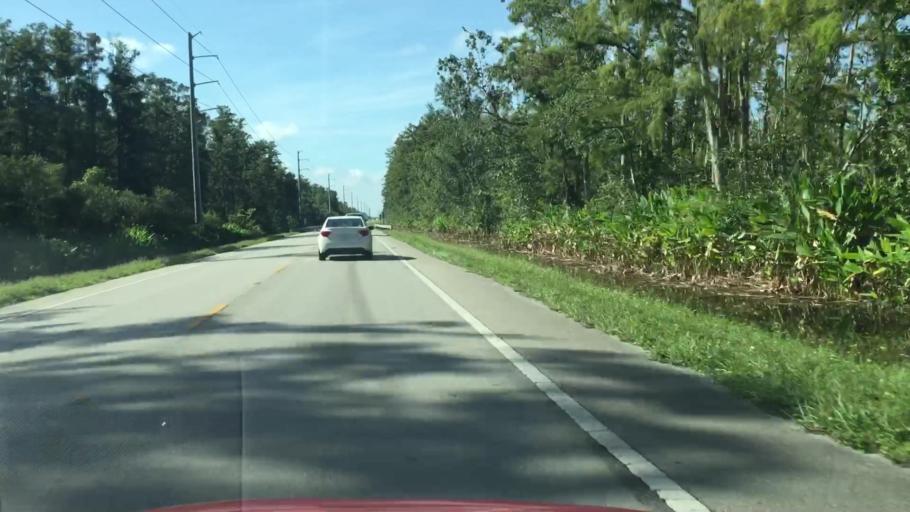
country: US
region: Florida
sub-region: Collier County
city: Orangetree
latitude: 26.3391
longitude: -81.5951
